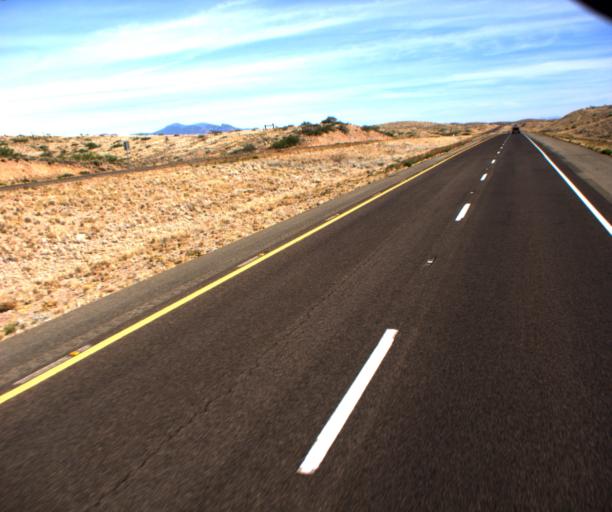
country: US
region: Arizona
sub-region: Cochise County
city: Willcox
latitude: 32.4112
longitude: -109.6618
